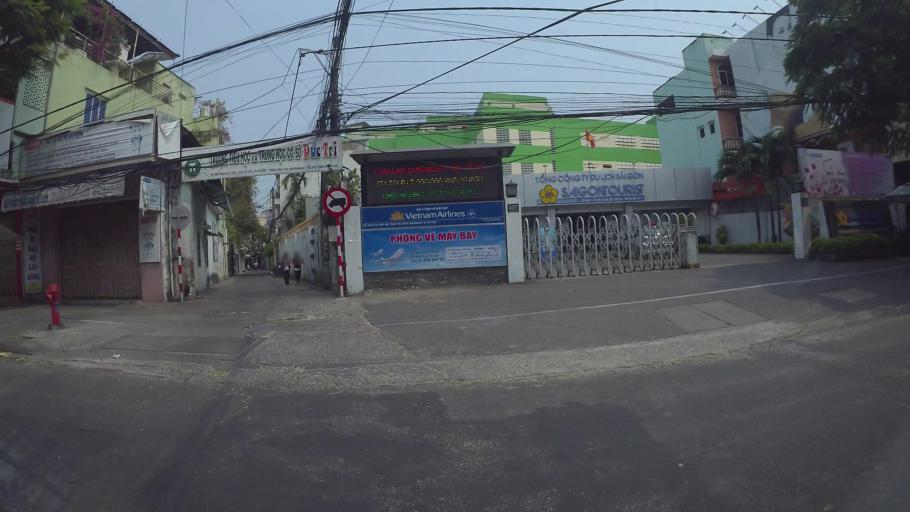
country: VN
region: Da Nang
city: Da Nang
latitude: 16.0571
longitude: 108.2189
